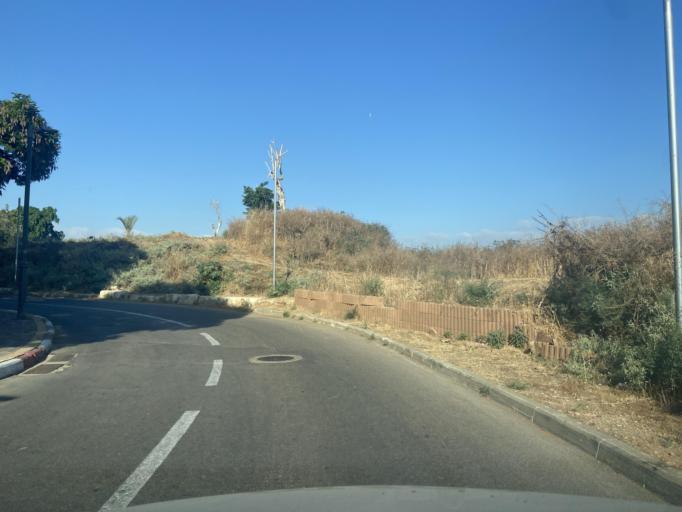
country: IL
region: Central District
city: Yehud
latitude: 32.0411
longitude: 34.8921
